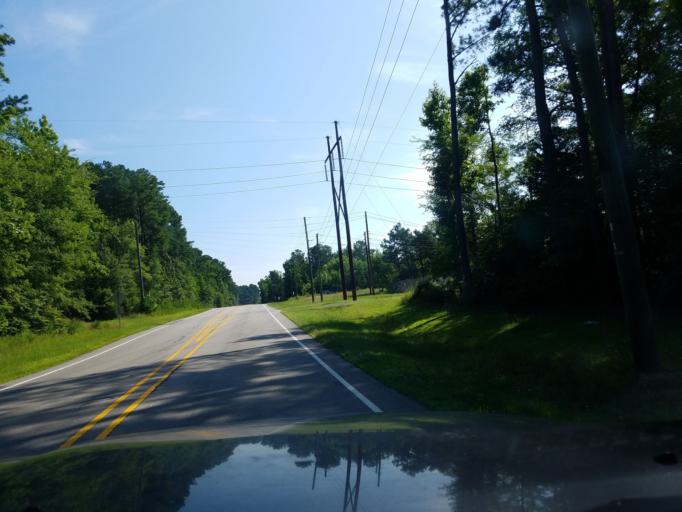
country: US
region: North Carolina
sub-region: Granville County
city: Oxford
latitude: 36.2966
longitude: -78.6160
